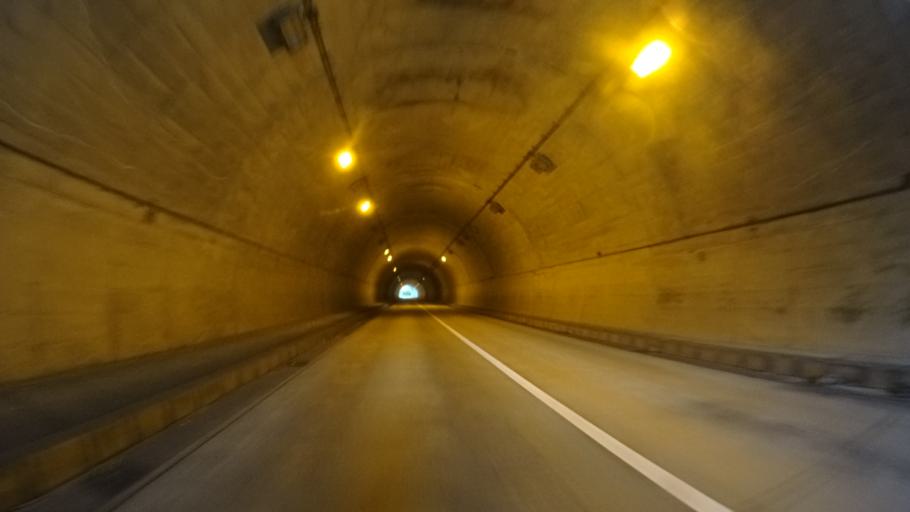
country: JP
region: Ishikawa
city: Hakui
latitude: 37.0818
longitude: 136.7309
